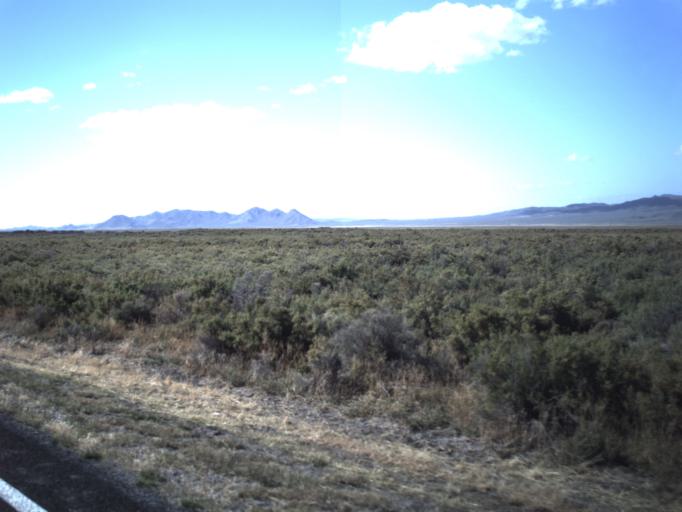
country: US
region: Utah
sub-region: Beaver County
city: Milford
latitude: 38.5604
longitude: -112.9910
